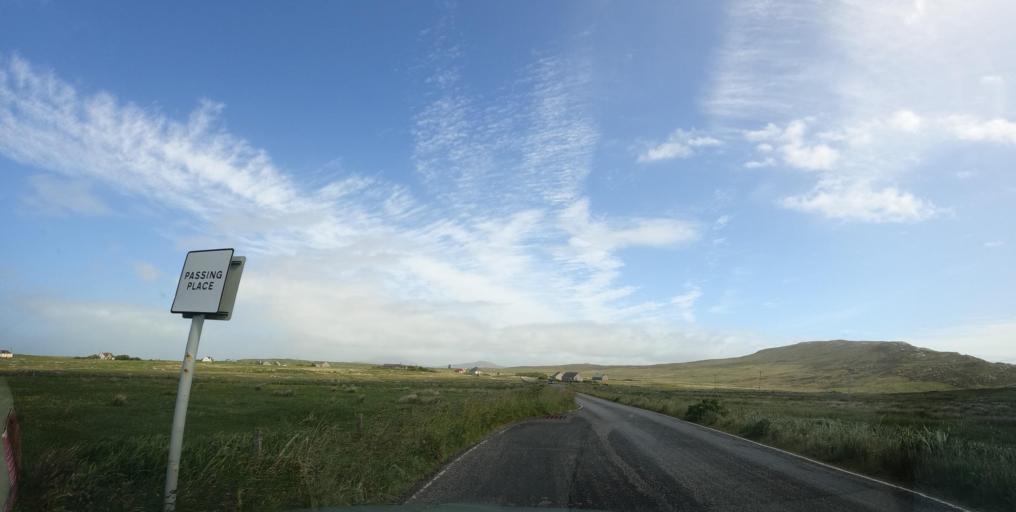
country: GB
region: Scotland
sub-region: Eilean Siar
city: Isle of South Uist
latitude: 57.1120
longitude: -7.3689
